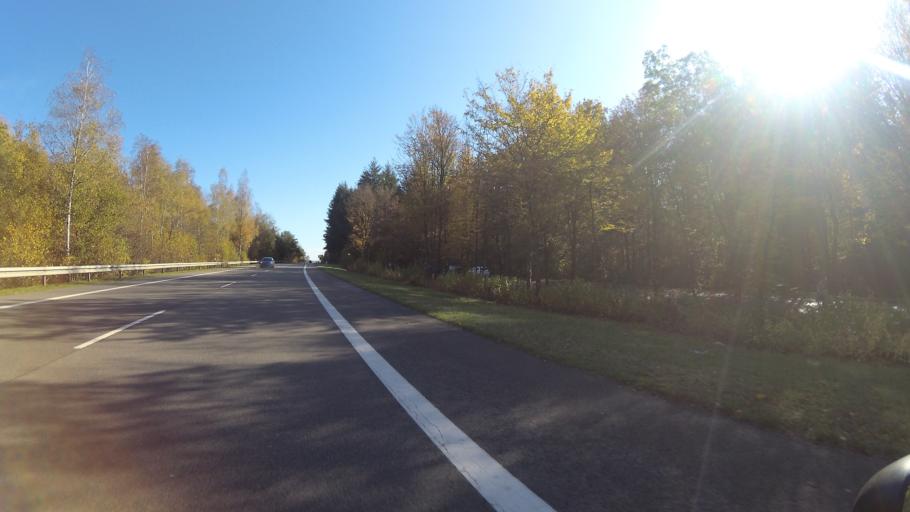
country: DE
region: Saarland
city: Losheim
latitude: 49.5207
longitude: 6.7206
